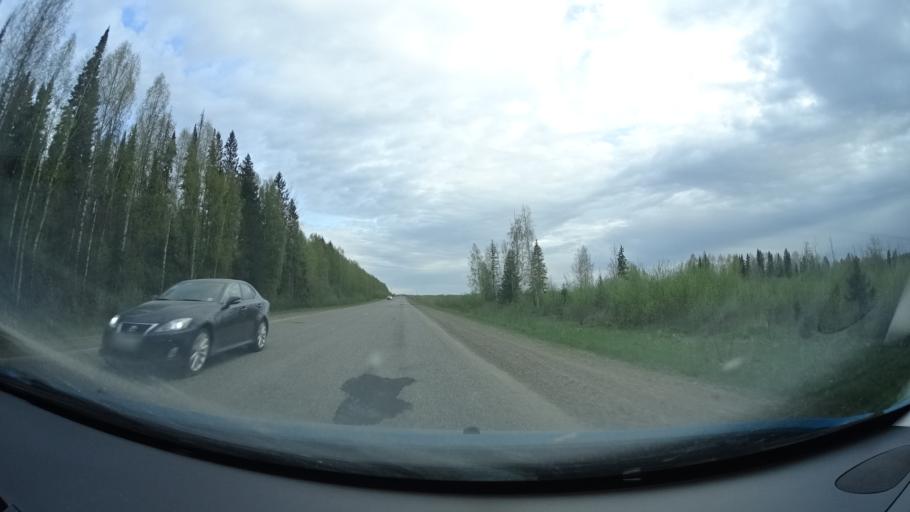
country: RU
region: Perm
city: Osa
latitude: 57.3847
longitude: 55.6088
